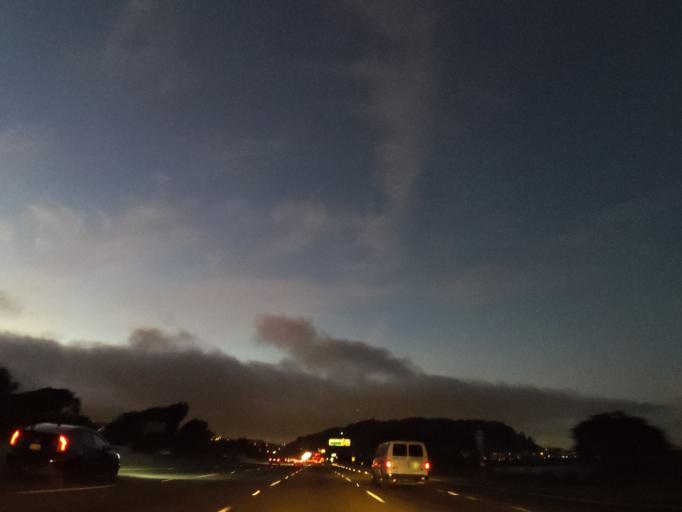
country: US
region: California
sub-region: San Mateo County
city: Brisbane
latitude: 37.6993
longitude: -122.3928
